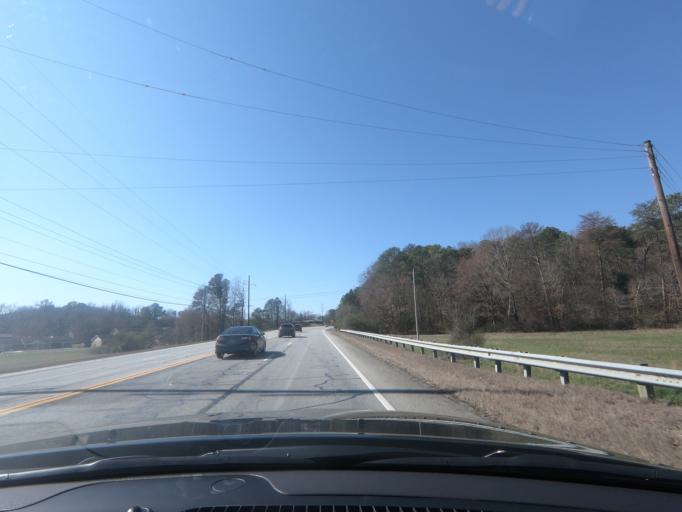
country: US
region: Georgia
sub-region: Gordon County
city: Calhoun
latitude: 34.4740
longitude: -84.9664
